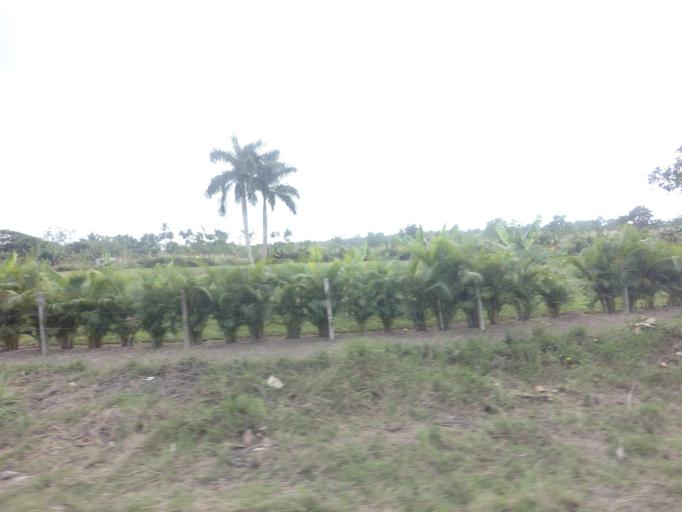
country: CU
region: Artemisa
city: Bauta
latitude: 23.0070
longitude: -82.5146
